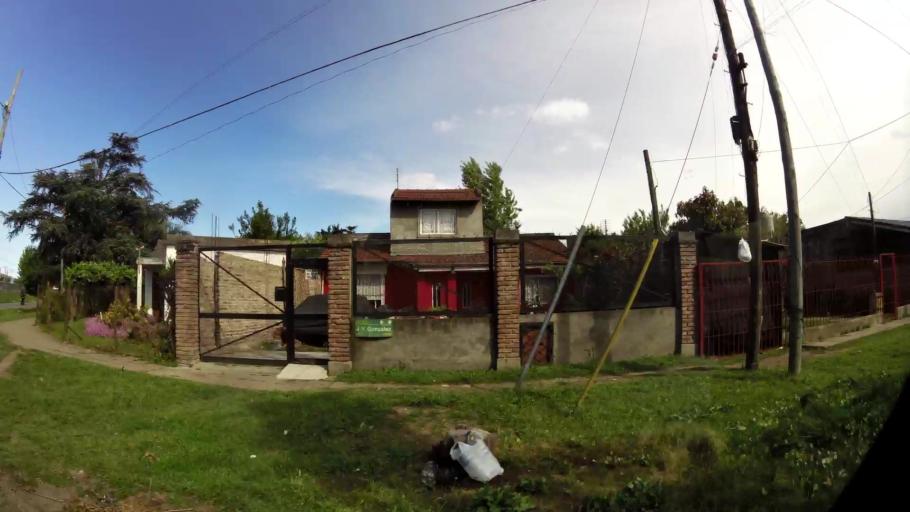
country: AR
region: Buenos Aires
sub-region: Partido de Almirante Brown
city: Adrogue
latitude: -34.8005
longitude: -58.3437
